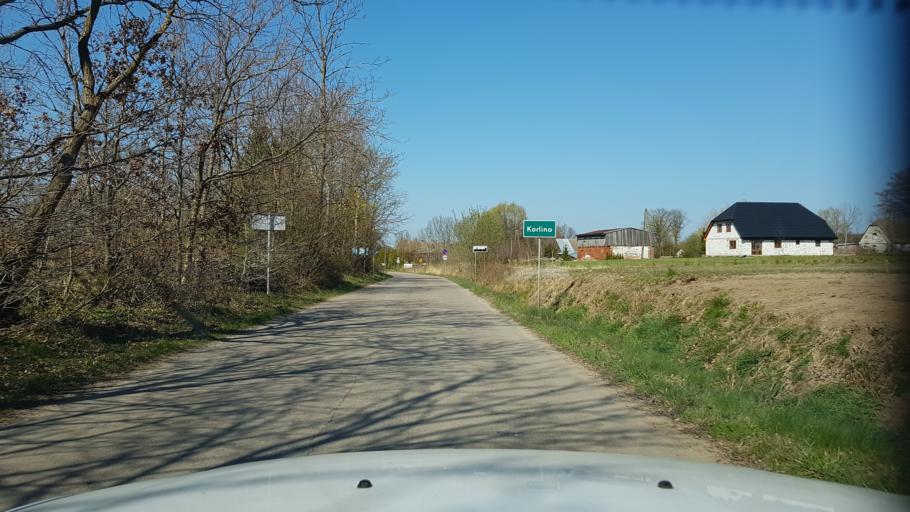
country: PL
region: West Pomeranian Voivodeship
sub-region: Powiat slawienski
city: Slawno
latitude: 54.5076
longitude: 16.6234
